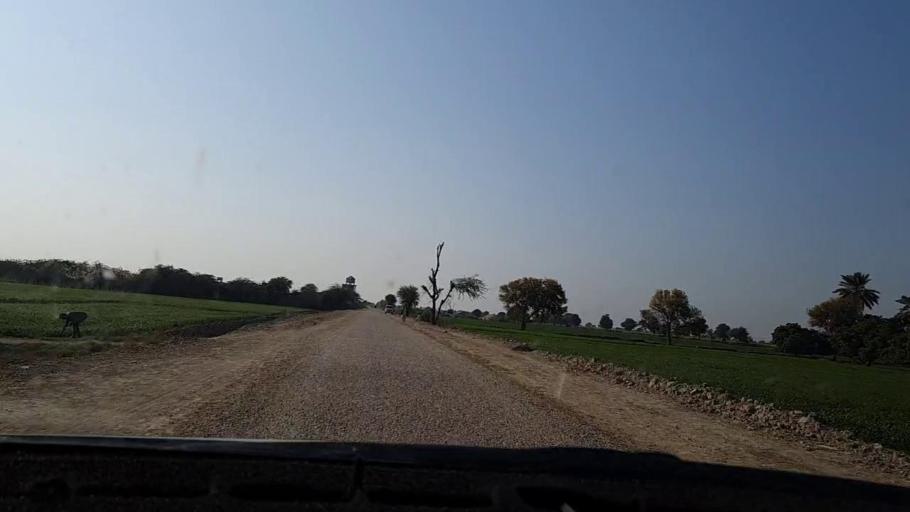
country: PK
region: Sindh
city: Tando Mittha Khan
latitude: 25.8284
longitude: 69.2857
